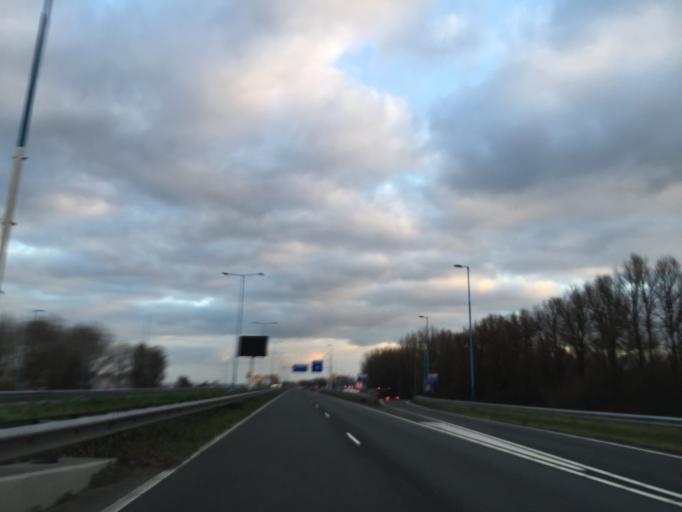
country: NL
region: South Holland
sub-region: Gemeente Zoetermeer
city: Zoetermeer
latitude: 52.0568
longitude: 4.5146
